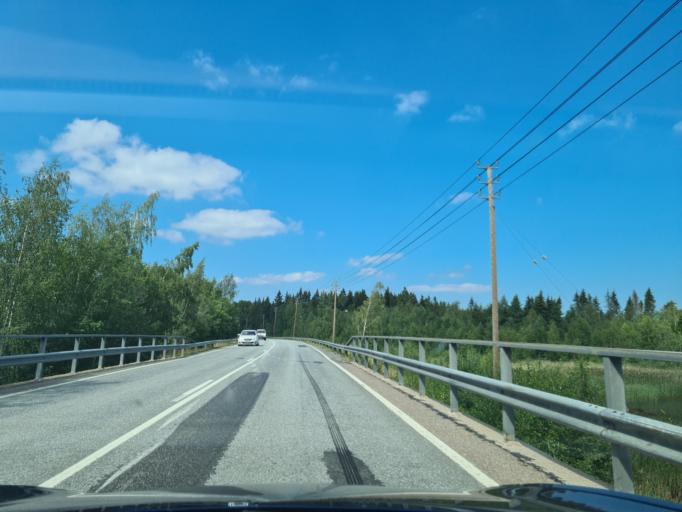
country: FI
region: Ostrobothnia
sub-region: Vaasa
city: Vaasa
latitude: 63.1889
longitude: 21.5651
